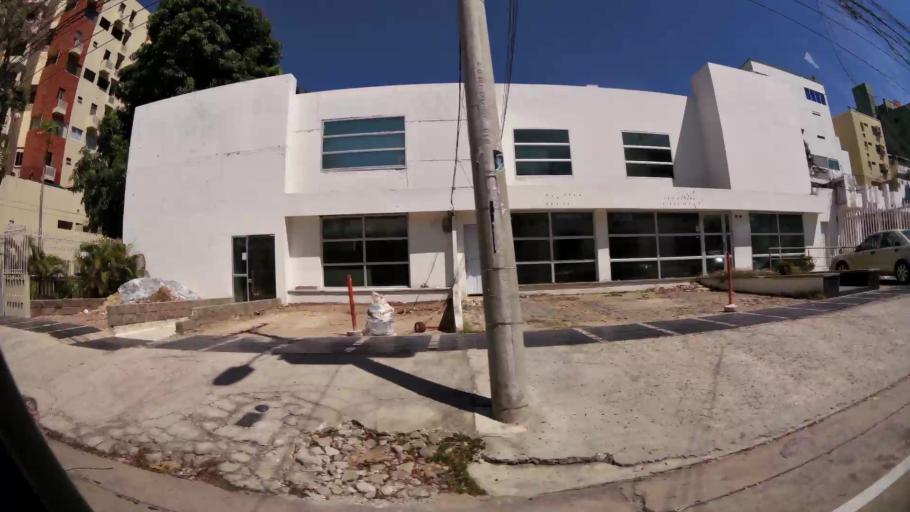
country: CO
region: Atlantico
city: Barranquilla
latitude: 11.0018
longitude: -74.8172
